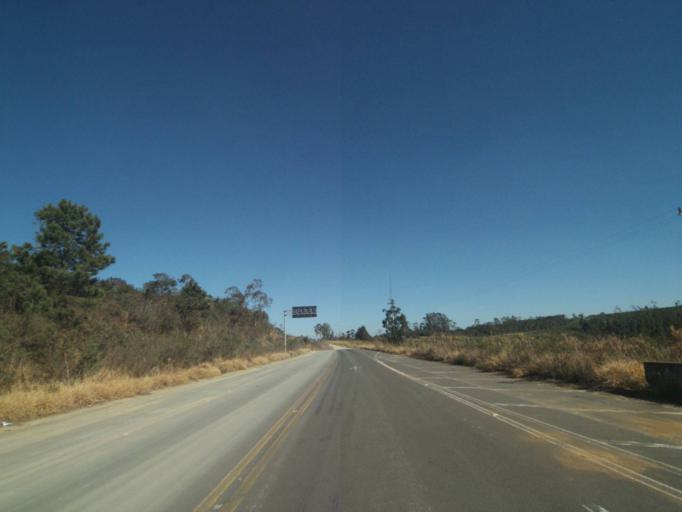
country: BR
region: Parana
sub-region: Tibagi
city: Tibagi
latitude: -24.8183
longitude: -50.4890
